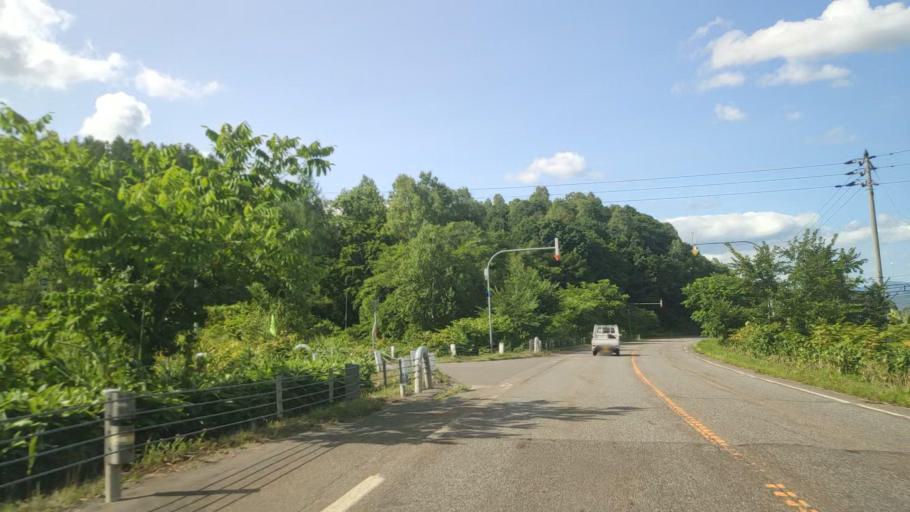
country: JP
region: Hokkaido
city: Nayoro
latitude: 44.3945
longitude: 142.3939
